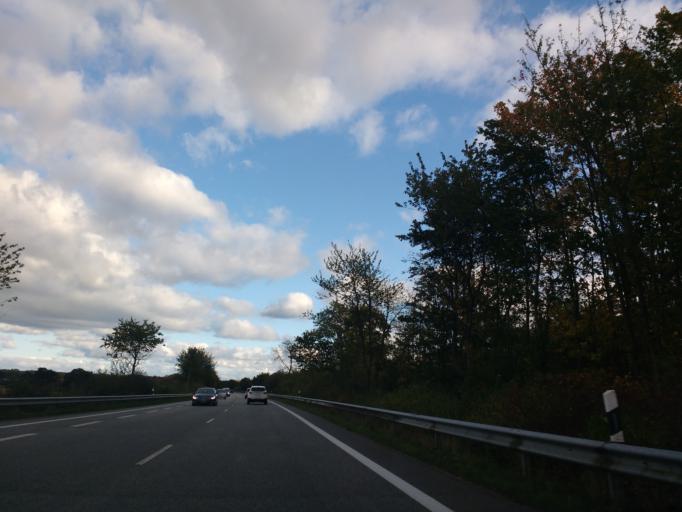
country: DE
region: Schleswig-Holstein
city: Altenkrempe
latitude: 54.1201
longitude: 10.8443
